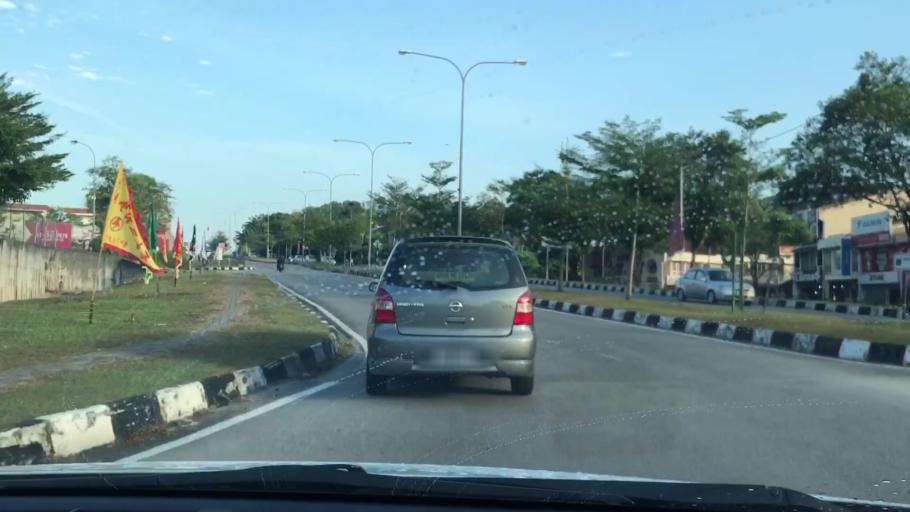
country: MY
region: Putrajaya
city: Putrajaya
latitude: 2.9942
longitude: 101.6730
